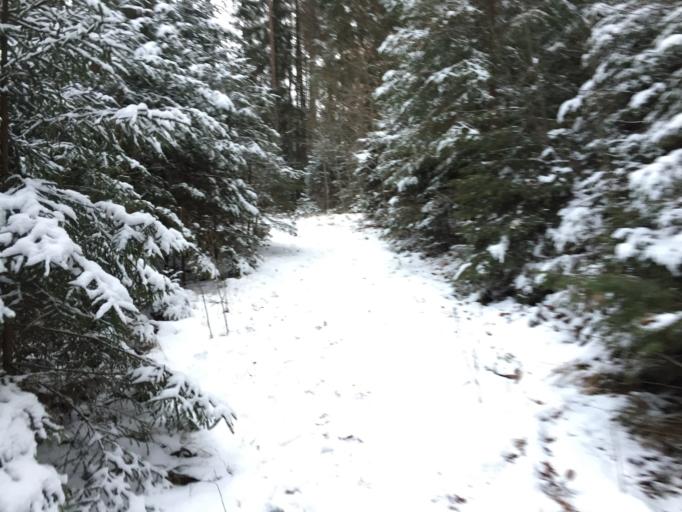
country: LV
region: Ligatne
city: Ligatne
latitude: 57.2414
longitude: 25.0495
